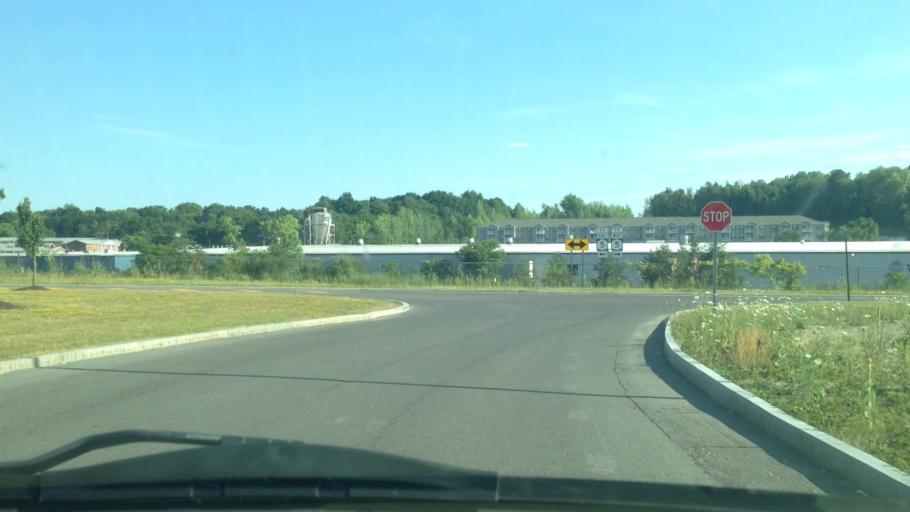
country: US
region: New York
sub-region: Onondaga County
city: Fairmount
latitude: 43.0554
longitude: -76.2726
